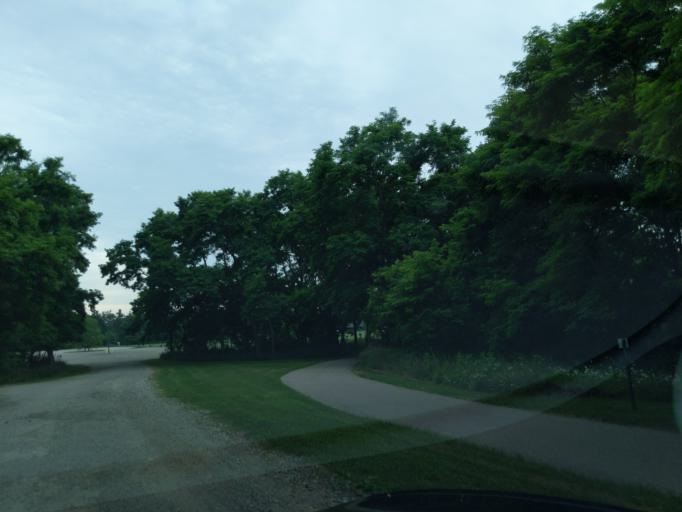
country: US
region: Michigan
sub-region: Livingston County
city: Whitmore Lake
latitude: 42.4501
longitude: -83.8220
